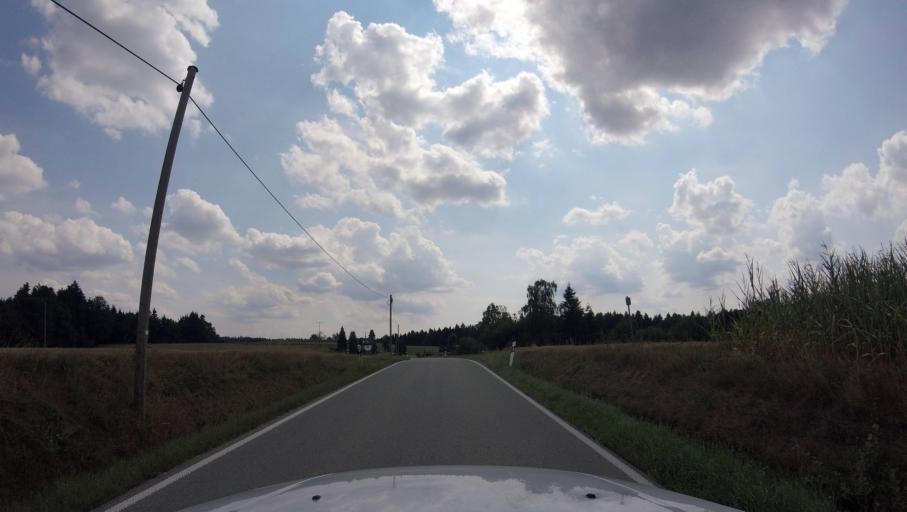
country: DE
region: Baden-Wuerttemberg
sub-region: Regierungsbezirk Stuttgart
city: Alfdorf
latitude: 48.8975
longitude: 9.6979
